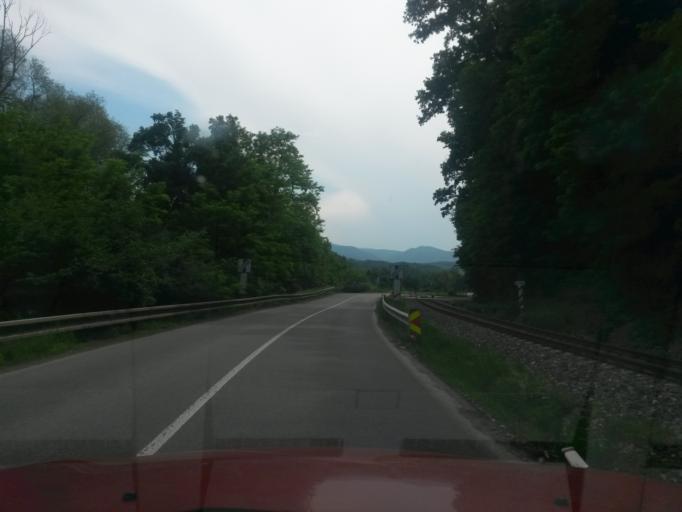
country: SK
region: Presovsky
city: Snina
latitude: 48.9905
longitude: 22.2140
